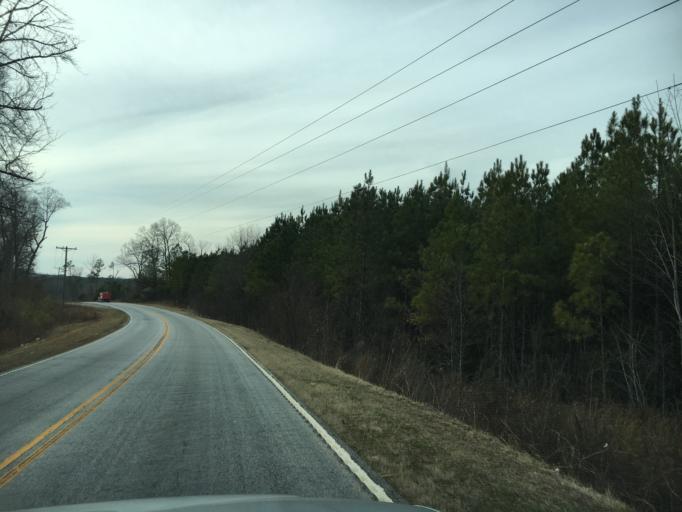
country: US
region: South Carolina
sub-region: Laurens County
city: Clinton
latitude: 34.5032
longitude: -81.8140
